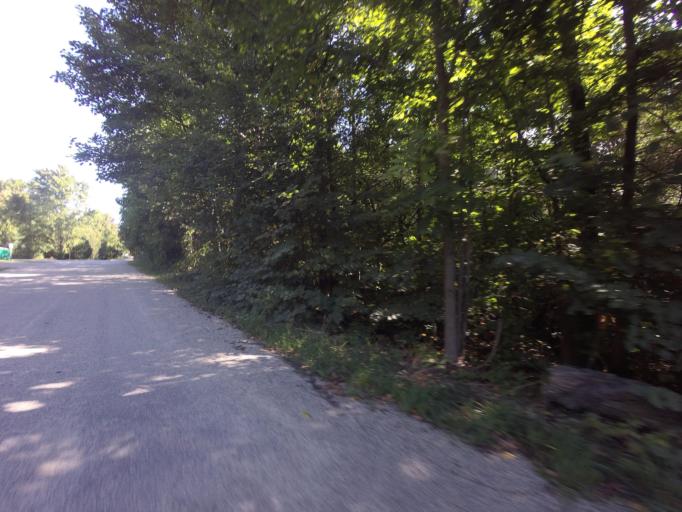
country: CA
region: Ontario
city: Waterloo
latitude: 43.6691
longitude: -80.4536
